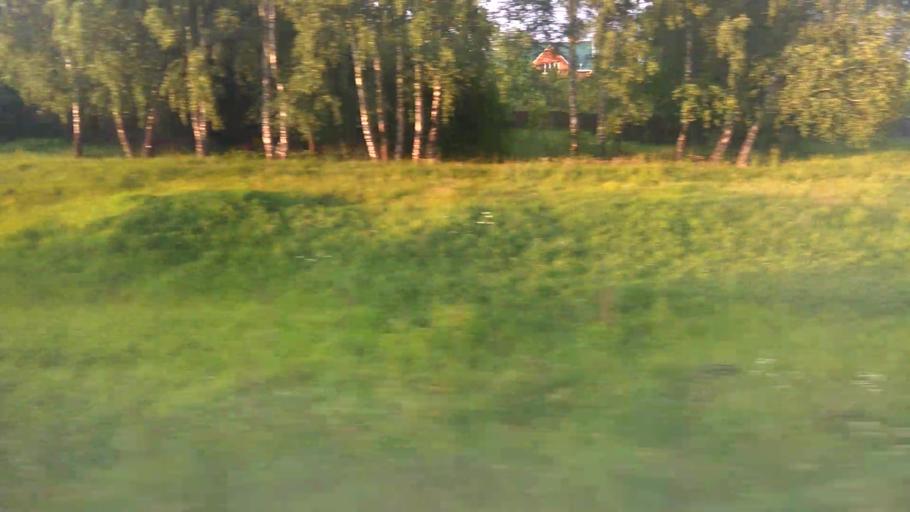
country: RU
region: Moskovskaya
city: Stupino
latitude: 54.8820
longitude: 38.1039
